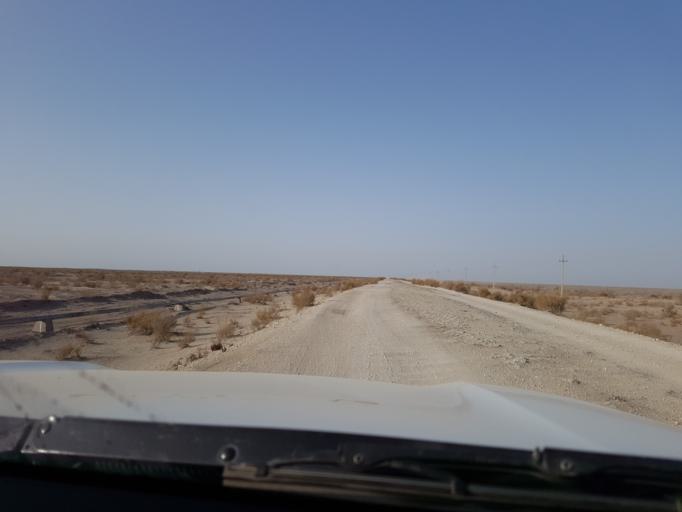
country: UZ
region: Karakalpakstan
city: Shumanay Shahri
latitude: 42.0038
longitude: 58.0713
